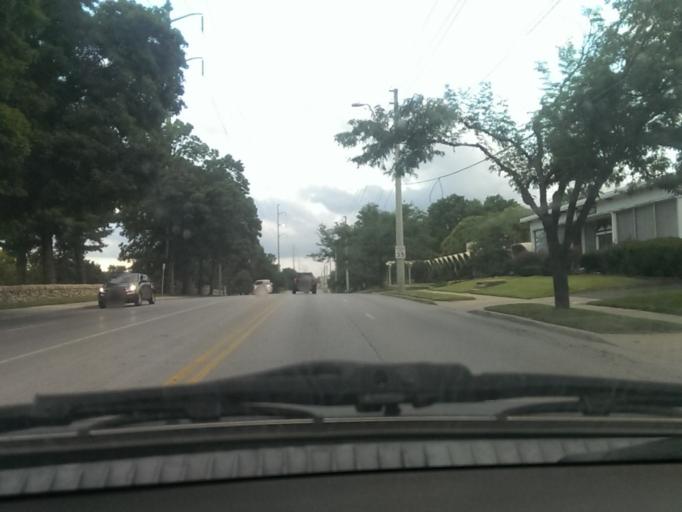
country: US
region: Kansas
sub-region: Johnson County
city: Mission Hills
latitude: 39.0038
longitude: -94.5752
